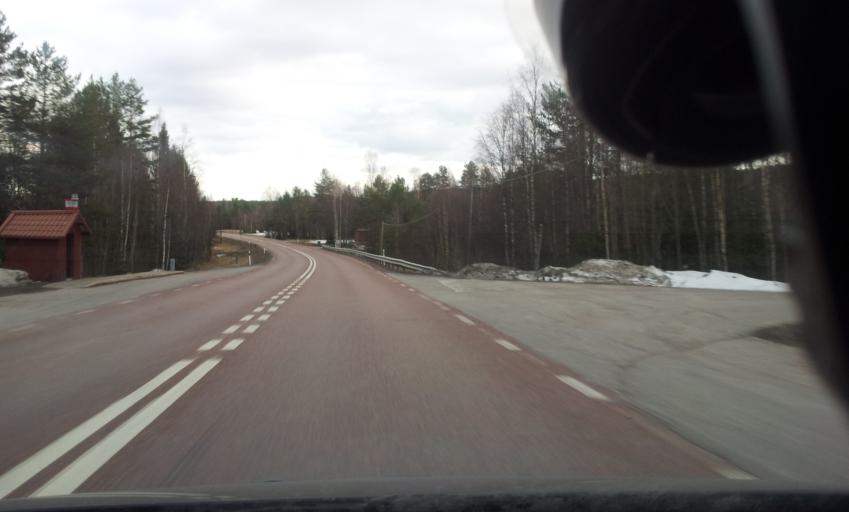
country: SE
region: Gaevleborg
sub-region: Ljusdals Kommun
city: Ljusdal
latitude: 61.7893
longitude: 16.1305
